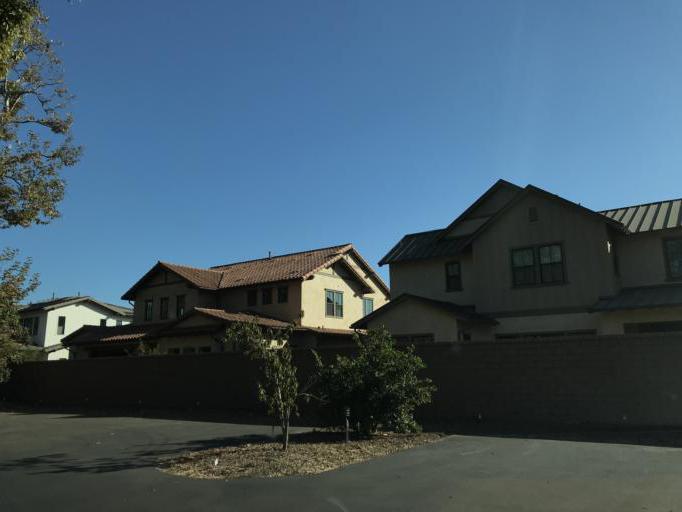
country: US
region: California
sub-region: Santa Barbara County
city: Goleta
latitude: 34.4515
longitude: -119.8139
